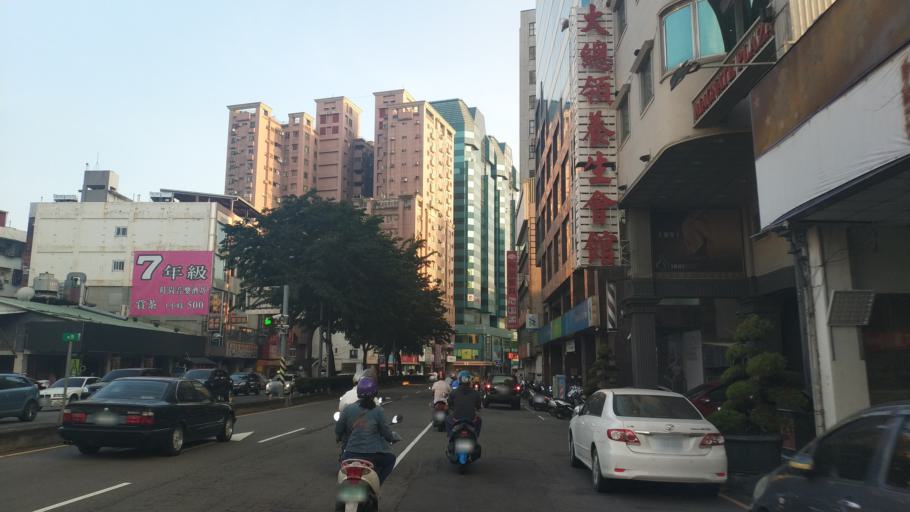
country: TW
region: Taiwan
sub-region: Taichung City
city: Taichung
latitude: 24.1555
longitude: 120.6770
